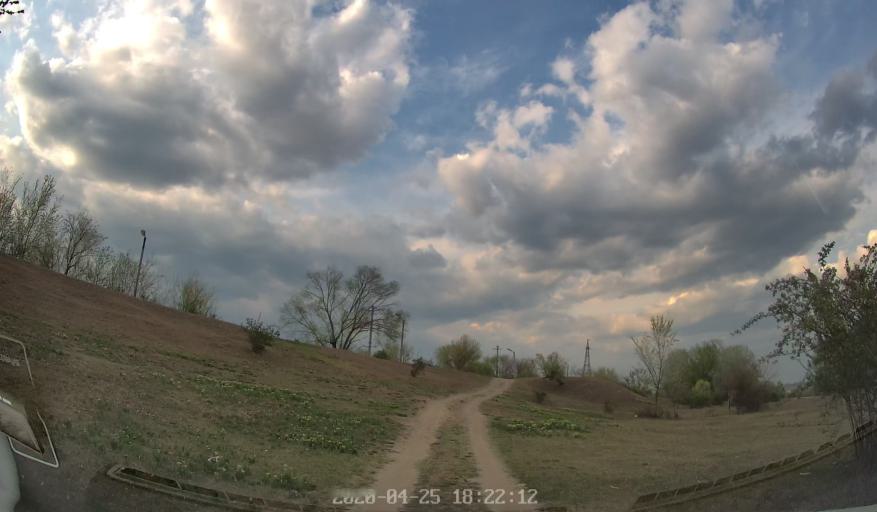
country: MD
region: Criuleni
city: Criuleni
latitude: 47.1563
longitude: 29.1323
